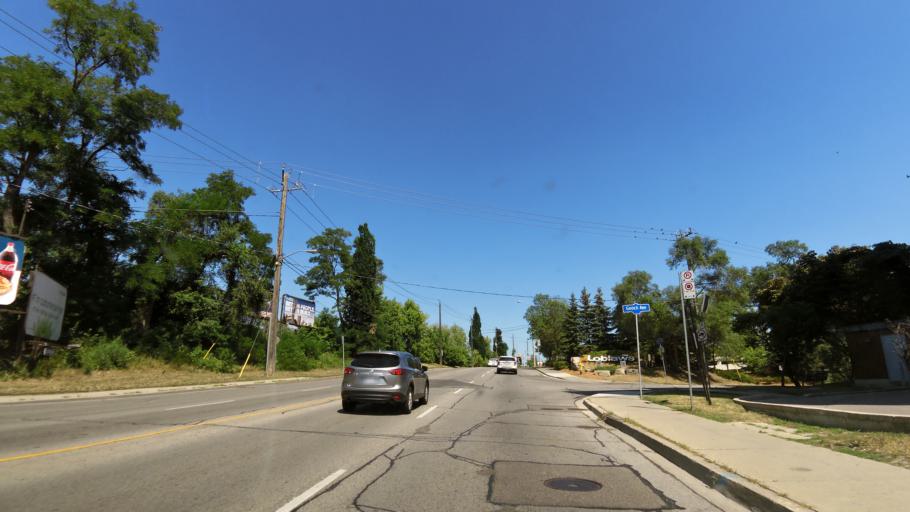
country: CA
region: Ontario
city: Etobicoke
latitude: 43.6655
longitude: -79.4990
